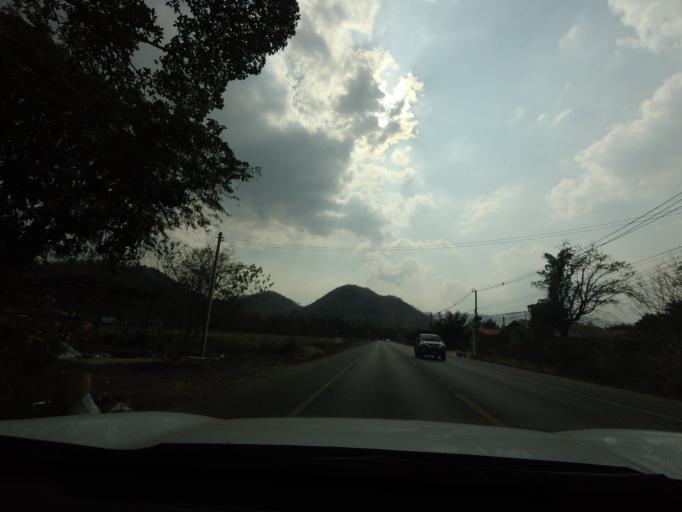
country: TH
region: Nakhon Ratchasima
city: Pak Chong
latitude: 14.5191
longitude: 101.3930
